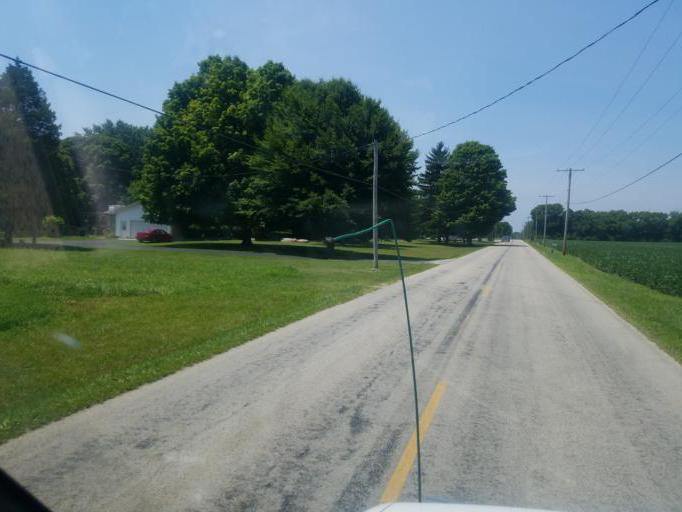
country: US
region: Ohio
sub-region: Shelby County
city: Sidney
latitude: 40.3028
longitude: -84.1208
